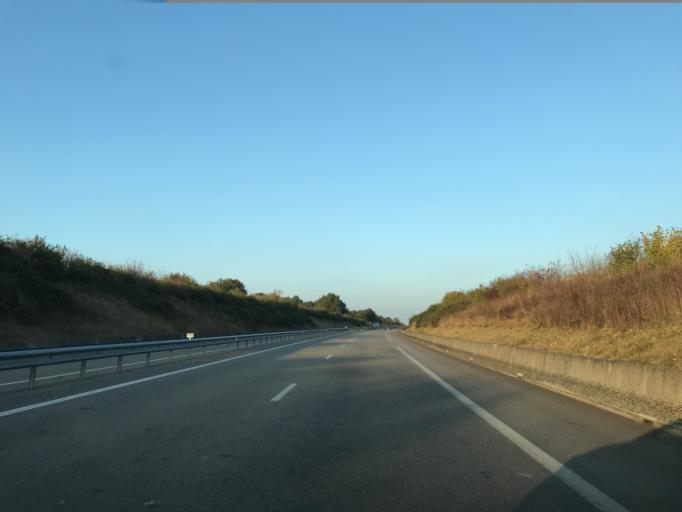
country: FR
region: Lower Normandy
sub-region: Departement de l'Orne
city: Sees
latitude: 48.4962
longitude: 0.2992
